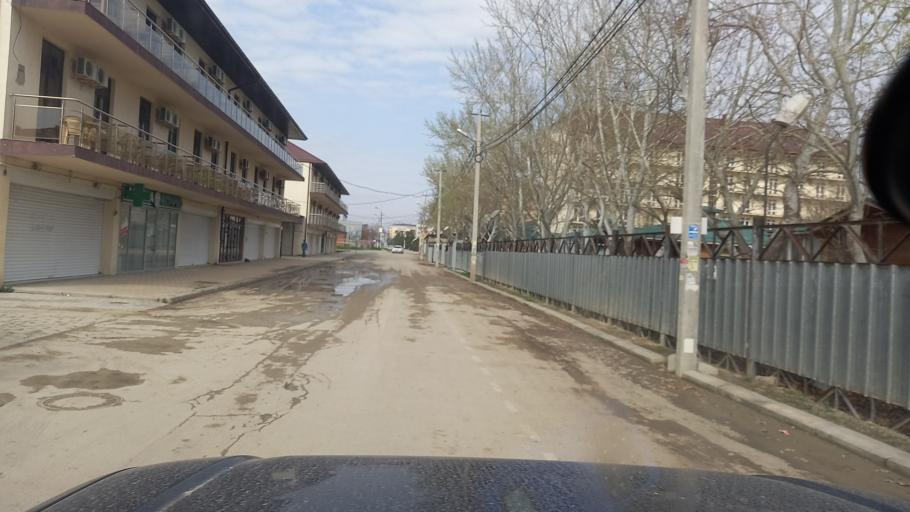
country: RU
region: Krasnodarskiy
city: Vityazevo
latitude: 44.9863
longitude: 37.2499
